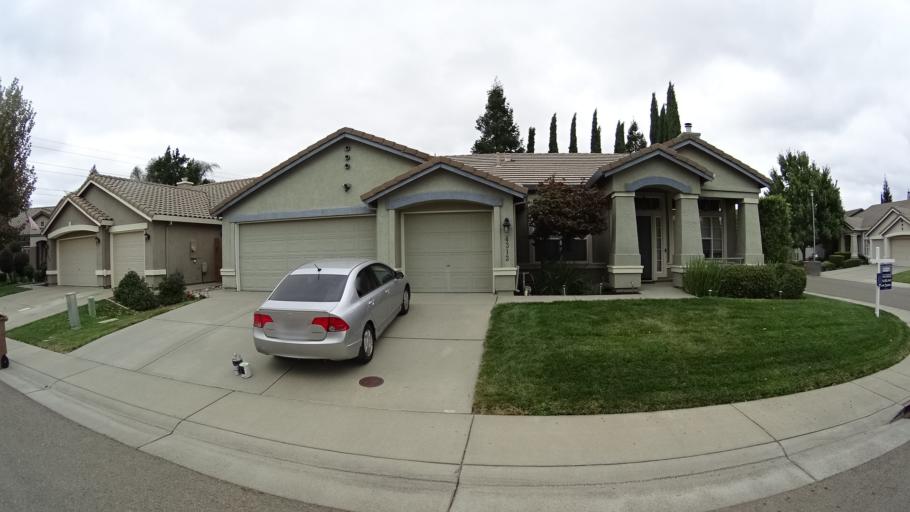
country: US
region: California
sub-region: Sacramento County
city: Laguna
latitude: 38.4172
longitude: -121.4542
